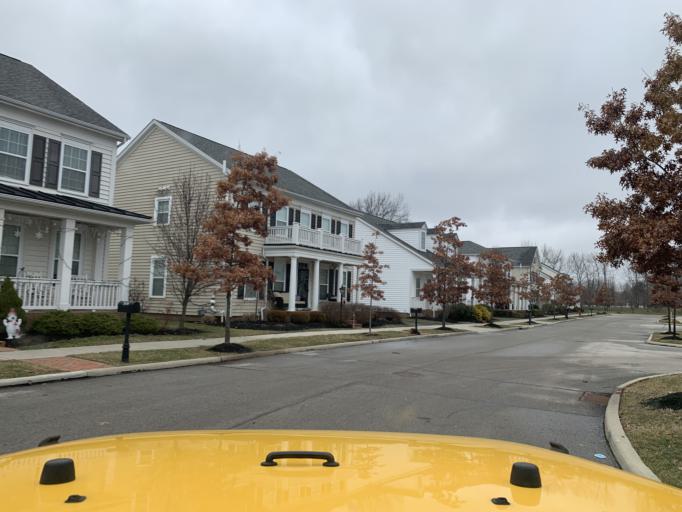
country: US
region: Ohio
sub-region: Franklin County
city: New Albany
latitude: 40.0890
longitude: -82.8081
